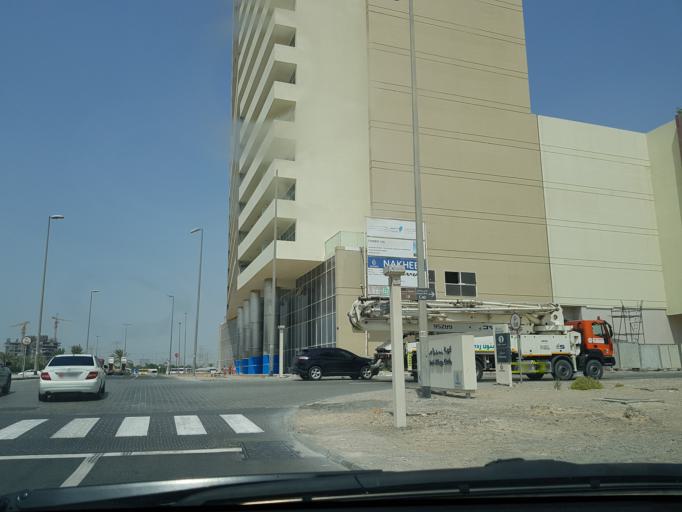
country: AE
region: Dubai
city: Dubai
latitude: 25.0527
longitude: 55.1977
